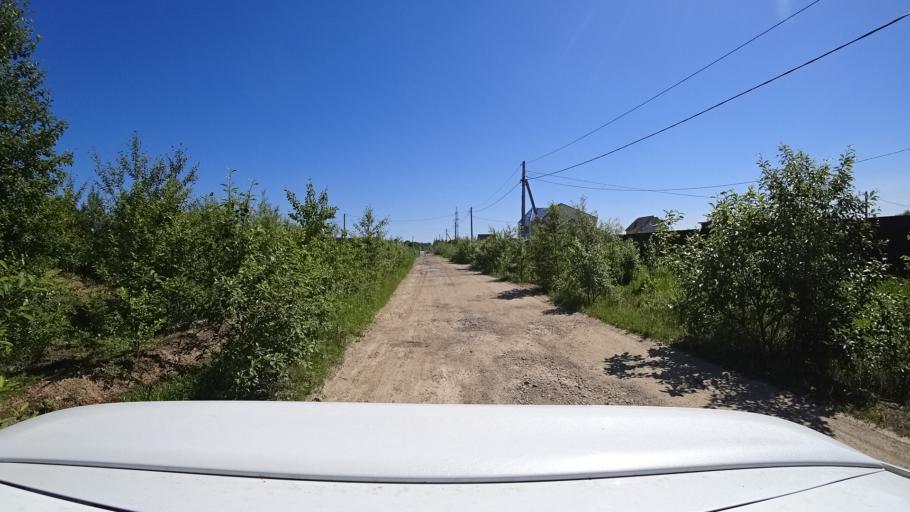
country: RU
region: Khabarovsk Krai
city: Topolevo
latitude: 48.5647
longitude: 135.1927
